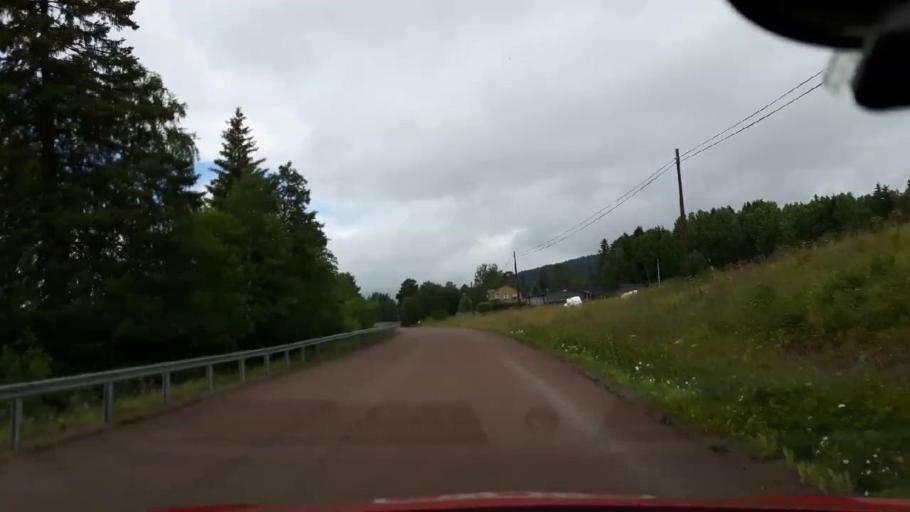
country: SE
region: Jaemtland
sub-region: Krokoms Kommun
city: Valla
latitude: 63.3744
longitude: 14.0246
